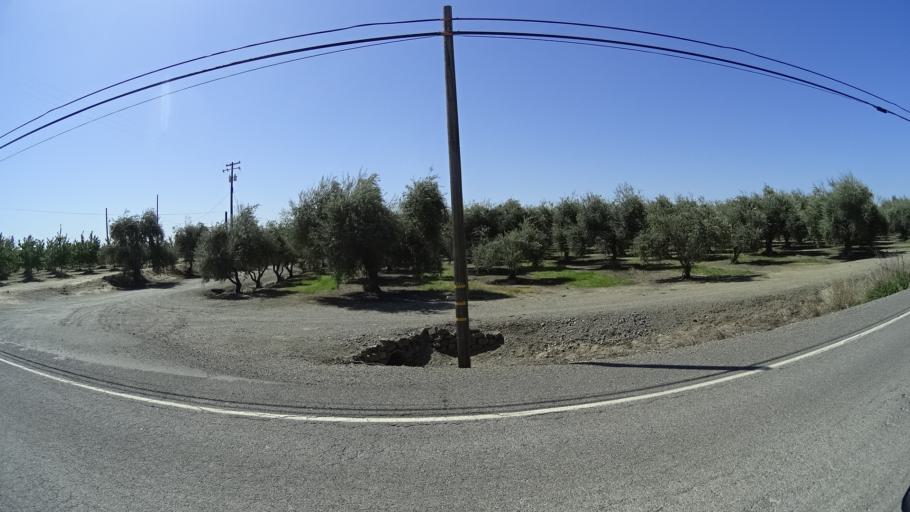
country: US
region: California
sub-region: Glenn County
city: Orland
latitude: 39.7105
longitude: -122.1232
